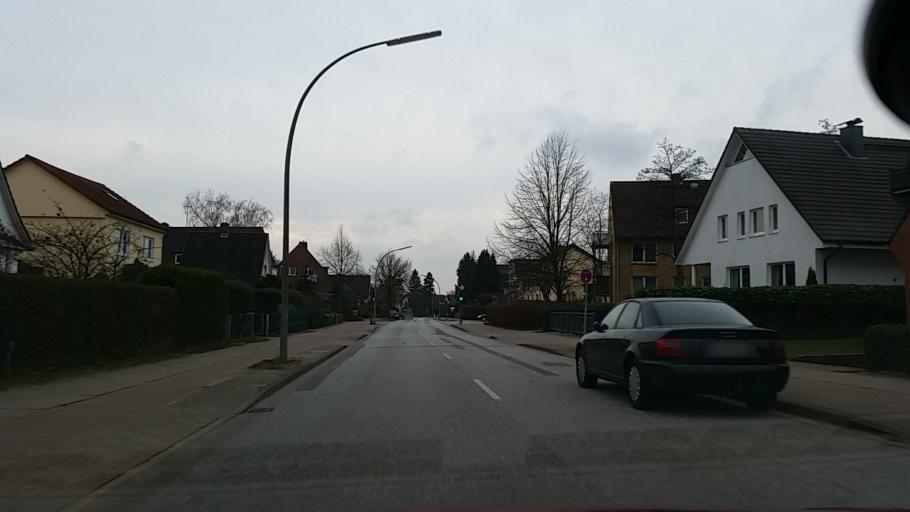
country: DE
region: Hamburg
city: Stellingen
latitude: 53.6322
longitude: 9.9517
